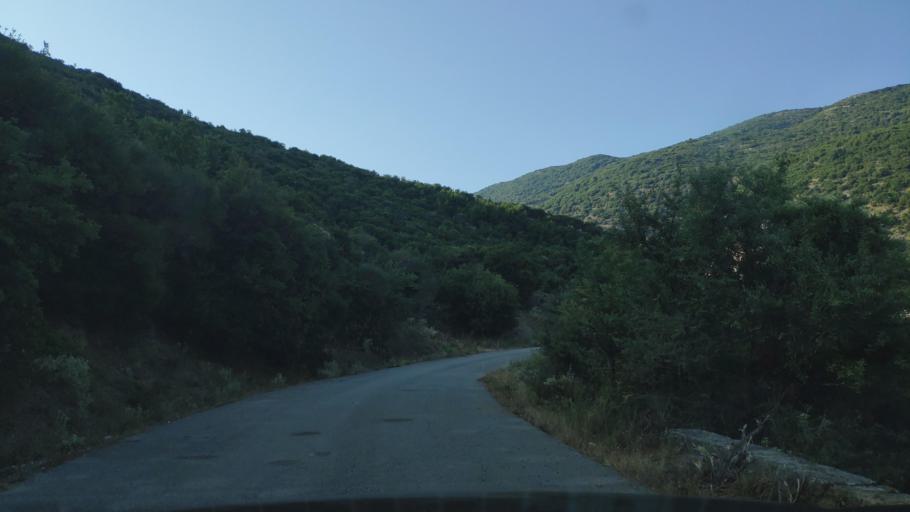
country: GR
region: West Greece
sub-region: Nomos Aitolias kai Akarnanias
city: Monastirakion
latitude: 38.8491
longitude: 20.9798
